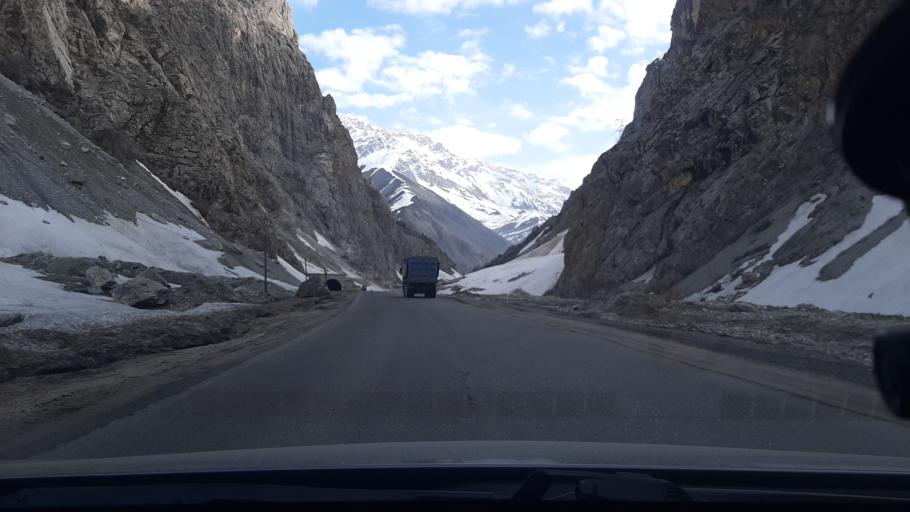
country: TJ
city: Tagob
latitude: 39.0076
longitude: 68.7773
